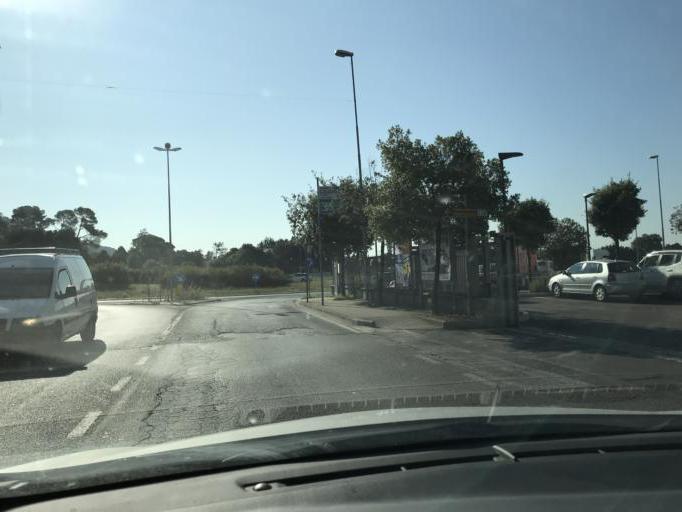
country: IT
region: Umbria
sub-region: Provincia di Perugia
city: Chiugiana-La Commenda
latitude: 43.0999
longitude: 12.3186
